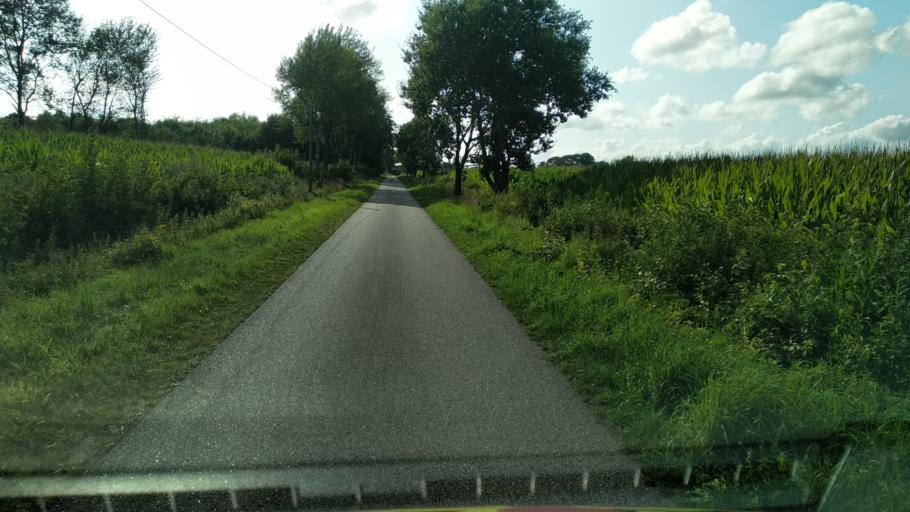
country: DE
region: Schleswig-Holstein
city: Gross Rheide
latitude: 54.4289
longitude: 9.4210
